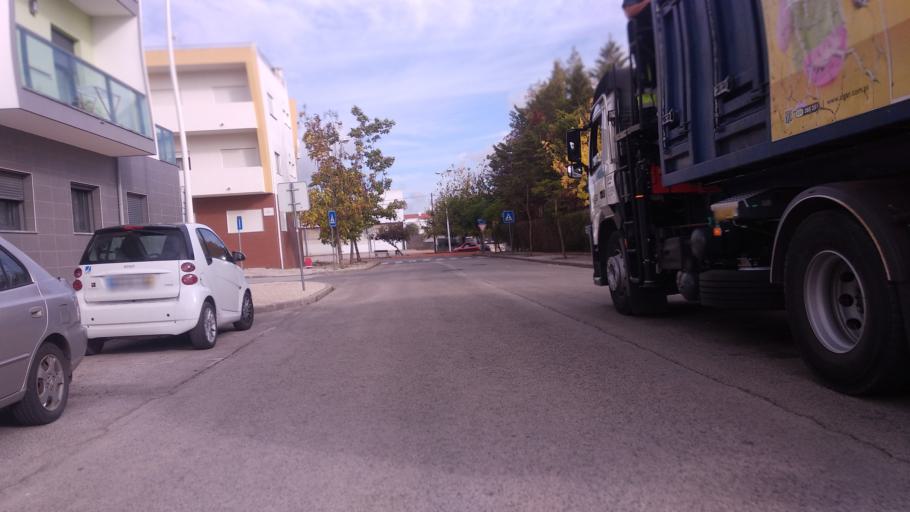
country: PT
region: Faro
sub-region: Sao Bras de Alportel
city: Sao Bras de Alportel
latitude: 37.1524
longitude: -7.8956
